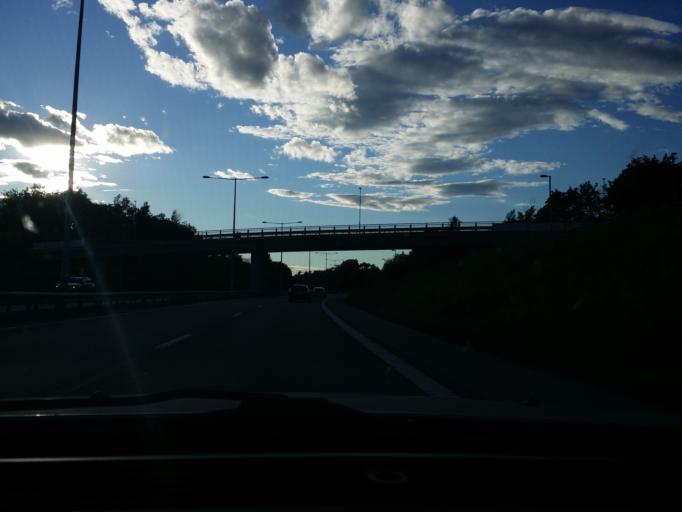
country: SE
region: Vaestmanland
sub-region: Vasteras
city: Vasteras
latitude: 59.6145
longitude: 16.5719
